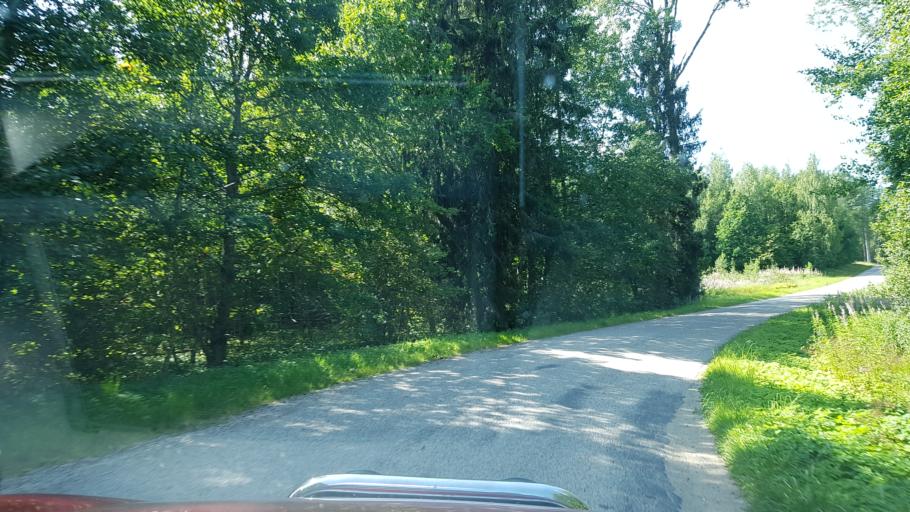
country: RU
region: Pskov
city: Pechory
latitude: 57.7066
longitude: 27.3130
